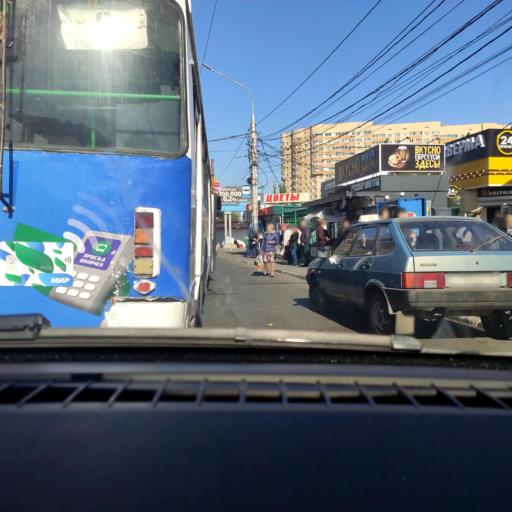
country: RU
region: Voronezj
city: Voronezh
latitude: 51.6714
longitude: 39.2522
